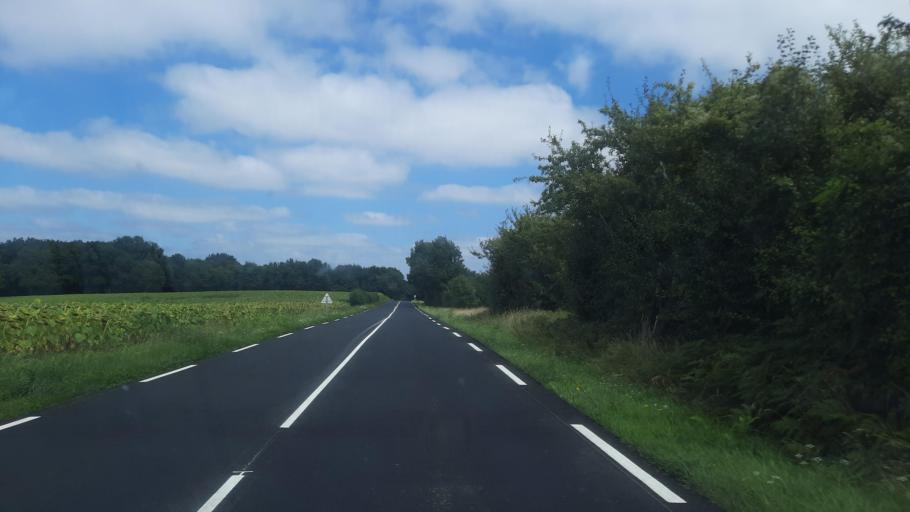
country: FR
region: Midi-Pyrenees
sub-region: Departement de la Haute-Garonne
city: Boulogne-sur-Gesse
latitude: 43.2945
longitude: 0.5829
